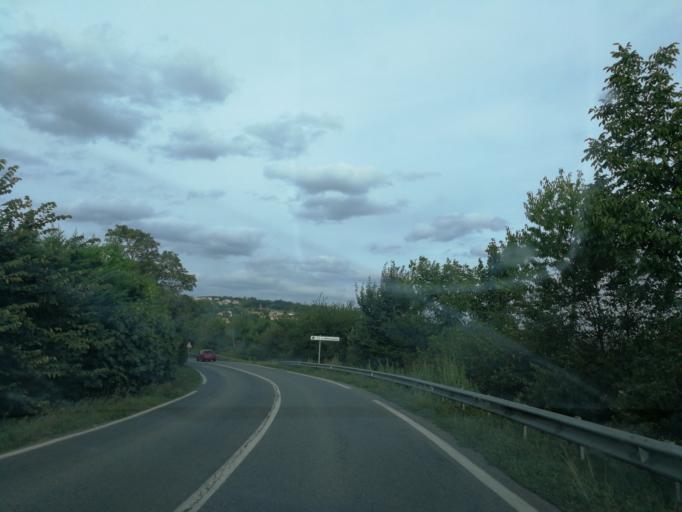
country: FR
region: Midi-Pyrenees
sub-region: Departement de la Haute-Garonne
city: Dremil-Lafage
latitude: 43.5929
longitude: 1.5910
